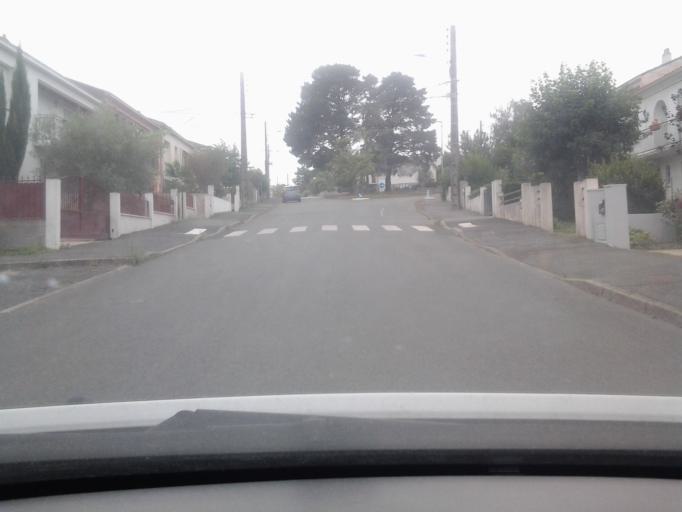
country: FR
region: Pays de la Loire
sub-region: Departement de la Vendee
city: La Roche-sur-Yon
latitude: 46.6612
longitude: -1.4281
